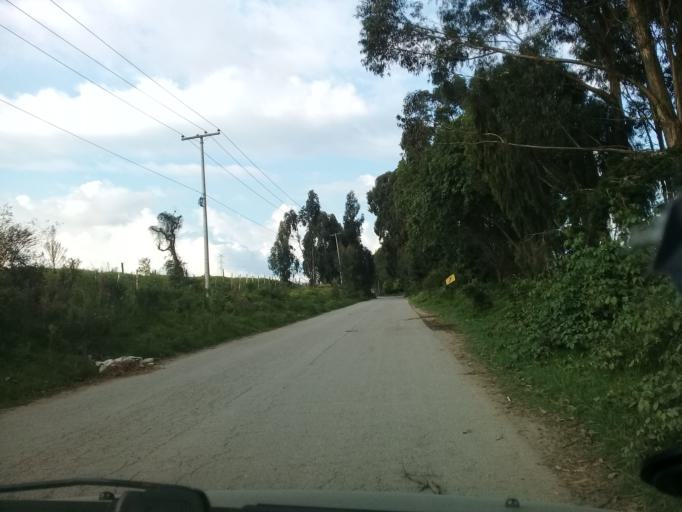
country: CO
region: Cundinamarca
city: Funza
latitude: 4.7757
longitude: -74.2209
